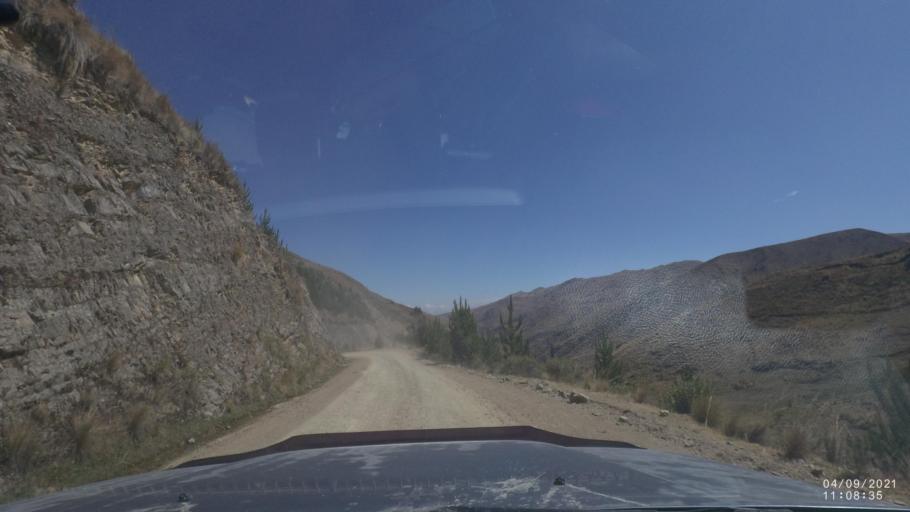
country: BO
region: Cochabamba
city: Sipe Sipe
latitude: -17.2818
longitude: -66.4763
